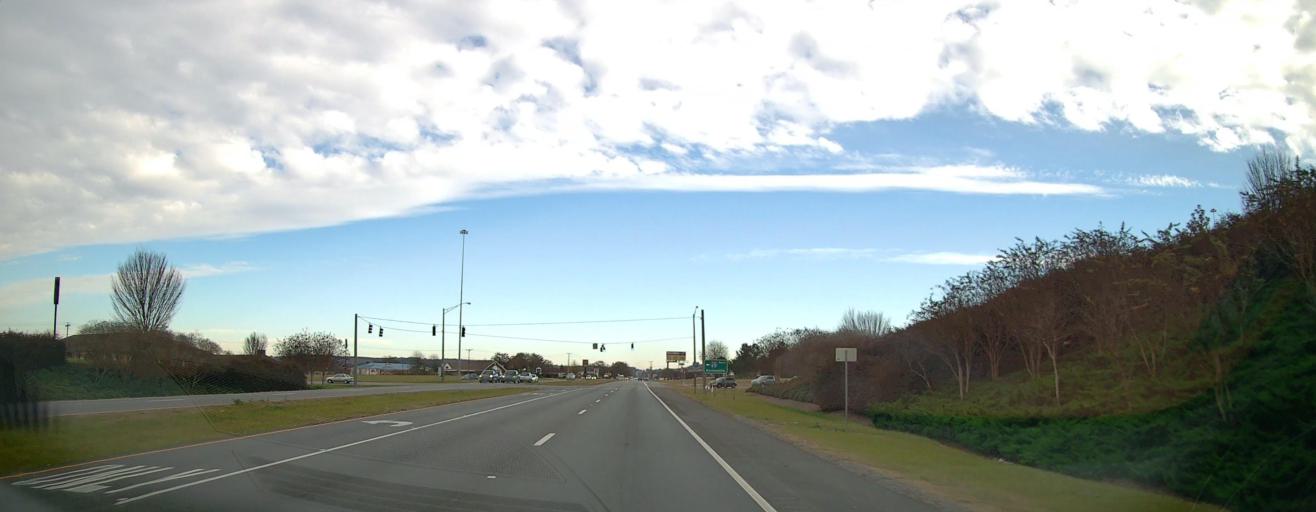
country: US
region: Alabama
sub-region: Morgan County
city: Priceville
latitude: 34.5330
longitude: -86.9054
